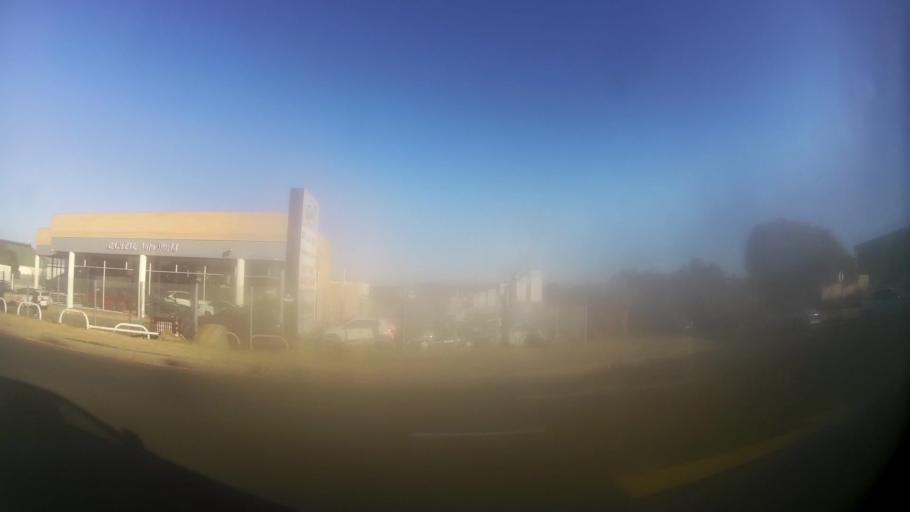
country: ZA
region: Gauteng
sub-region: City of Johannesburg Metropolitan Municipality
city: Midrand
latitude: -25.9894
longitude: 28.1305
